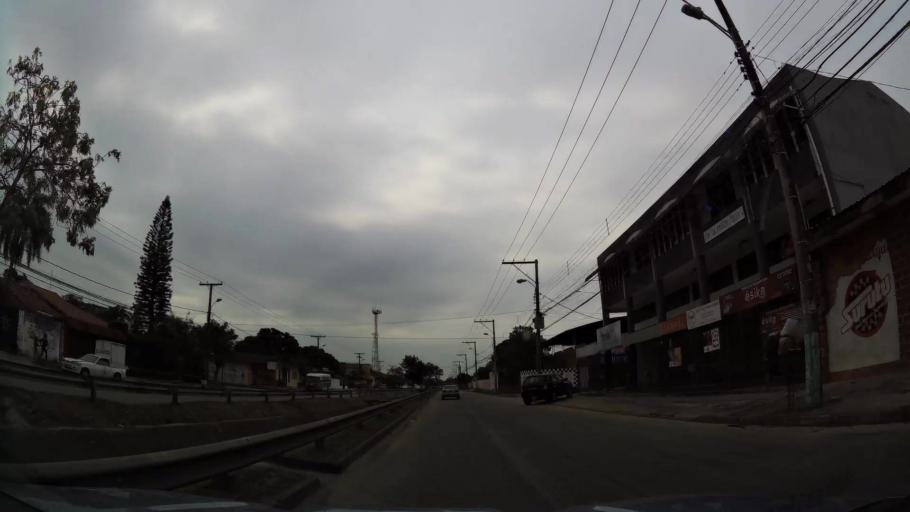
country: BO
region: Santa Cruz
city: Santa Cruz de la Sierra
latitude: -17.7556
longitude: -63.1818
